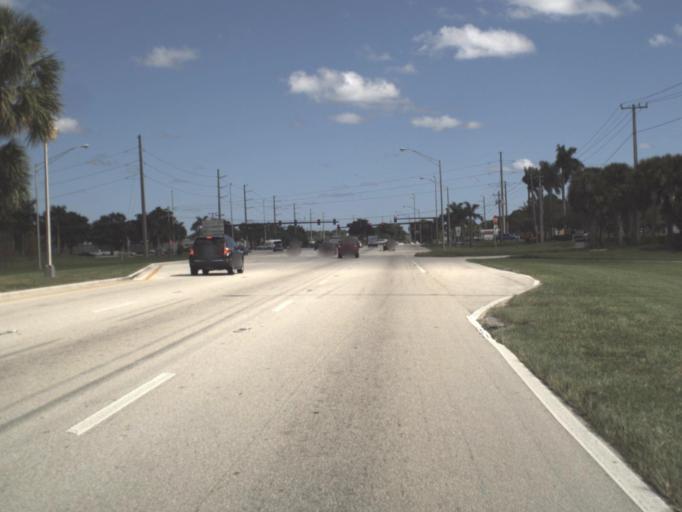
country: US
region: Florida
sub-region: Palm Beach County
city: Boca Pointe
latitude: 26.3042
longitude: -80.1550
